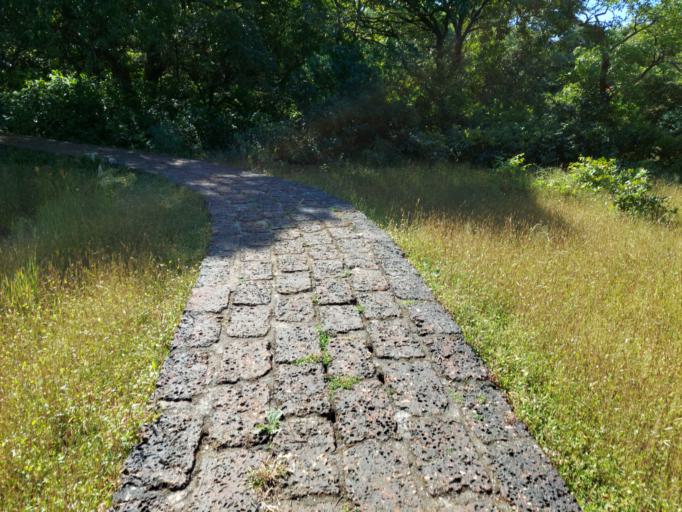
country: IN
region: Maharashtra
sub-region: Sindhudurg
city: Kudal
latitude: 16.0821
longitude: 73.8457
